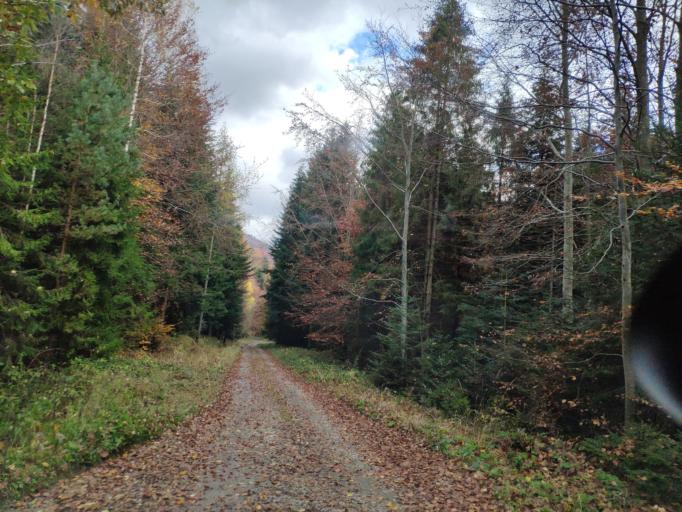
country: SK
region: Kosicky
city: Medzev
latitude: 48.7614
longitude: 20.9727
